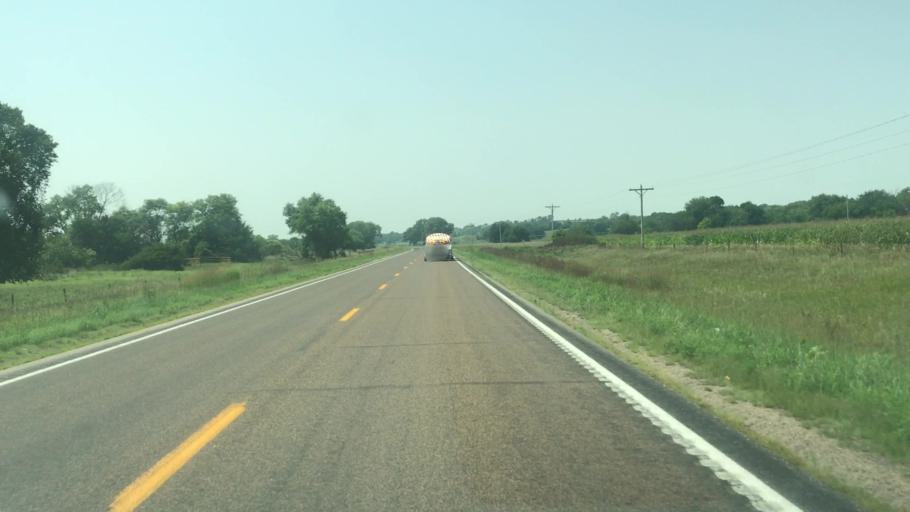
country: US
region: Nebraska
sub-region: Buffalo County
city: Ravenna
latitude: 41.0764
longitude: -98.6892
